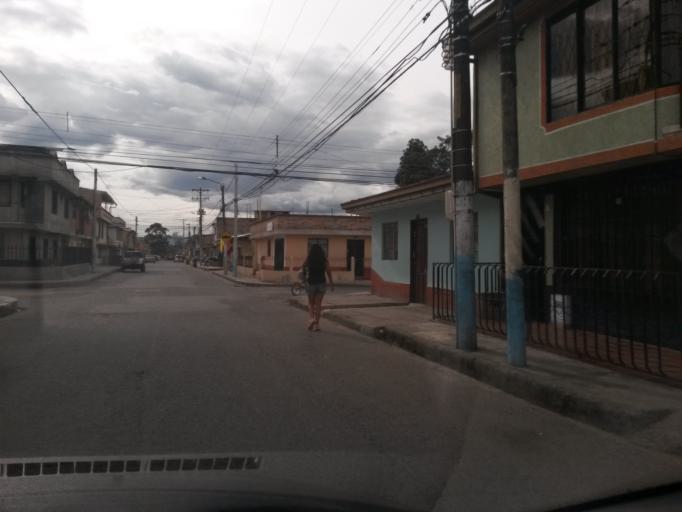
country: CO
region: Cauca
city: Popayan
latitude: 2.4517
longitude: -76.6266
